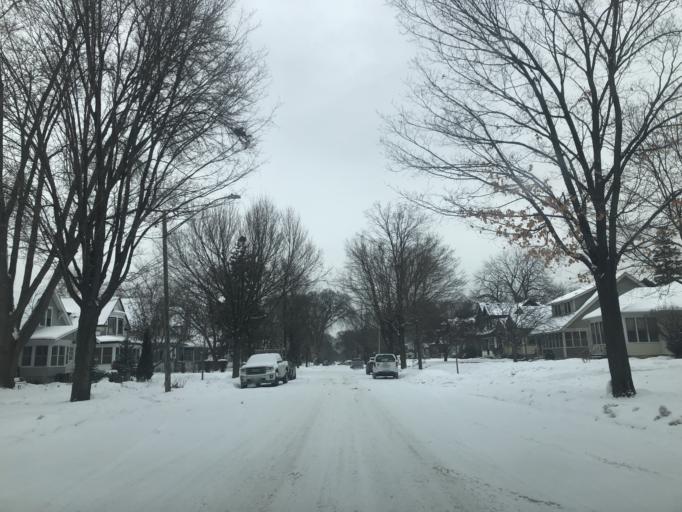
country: US
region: Minnesota
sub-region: Hennepin County
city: Richfield
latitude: 44.9273
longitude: -93.2831
